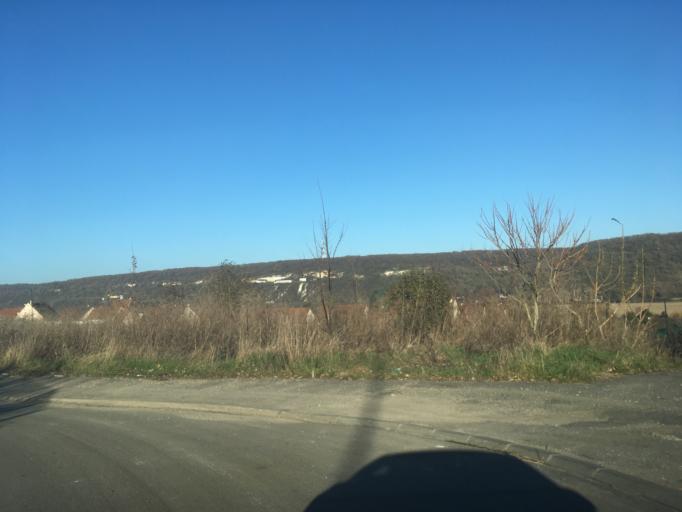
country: FR
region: Haute-Normandie
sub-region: Departement de l'Eure
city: Vernon
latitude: 49.0789
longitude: 1.5019
